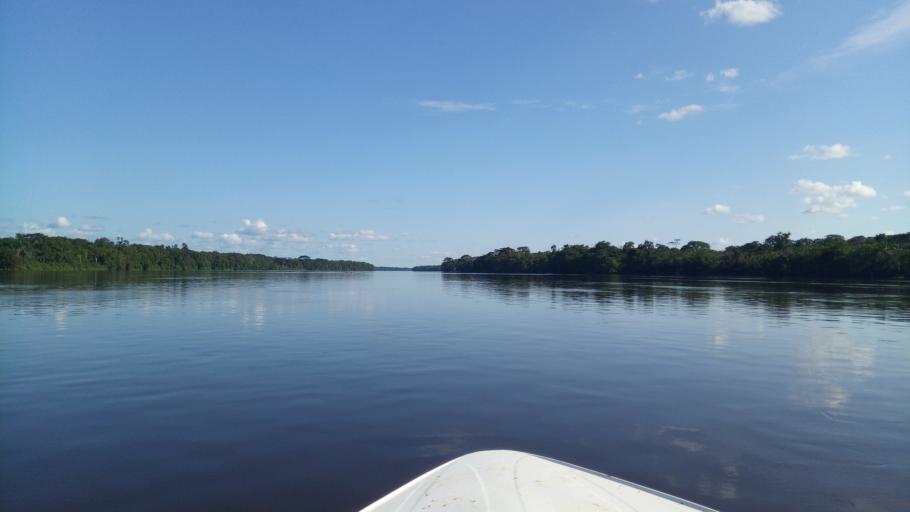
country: CD
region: Eastern Province
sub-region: Sous-Region de la Tshopo
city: Yangambi
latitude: 0.4444
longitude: 24.1630
